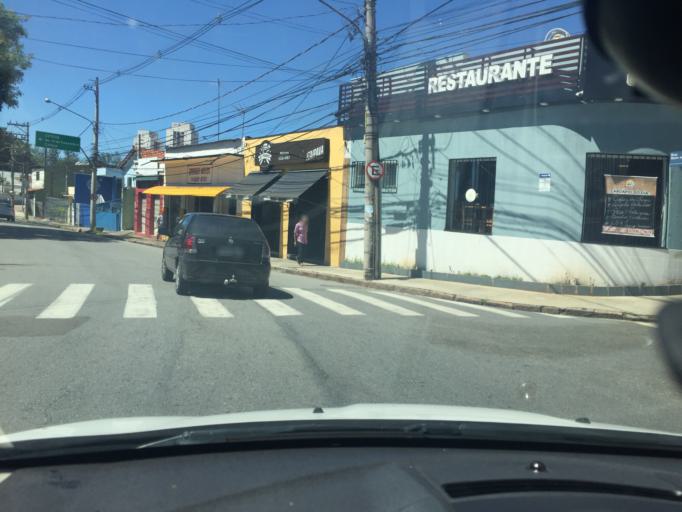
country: BR
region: Sao Paulo
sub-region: Jundiai
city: Jundiai
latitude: -23.2063
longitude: -46.8860
